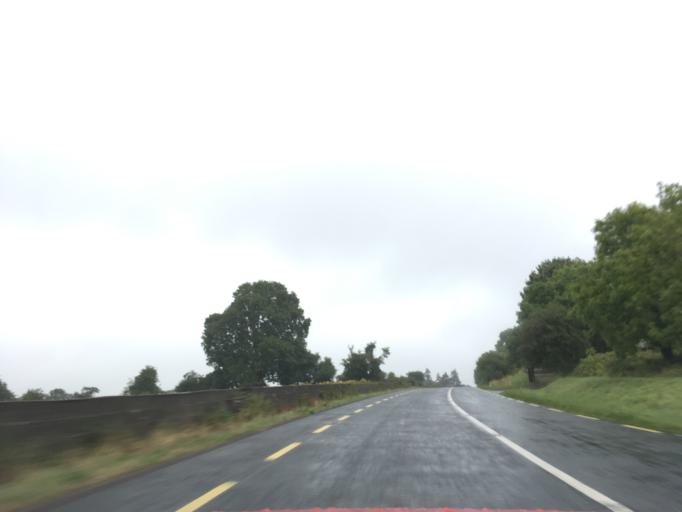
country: IE
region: Munster
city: Tipperary
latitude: 52.4819
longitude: -8.0931
